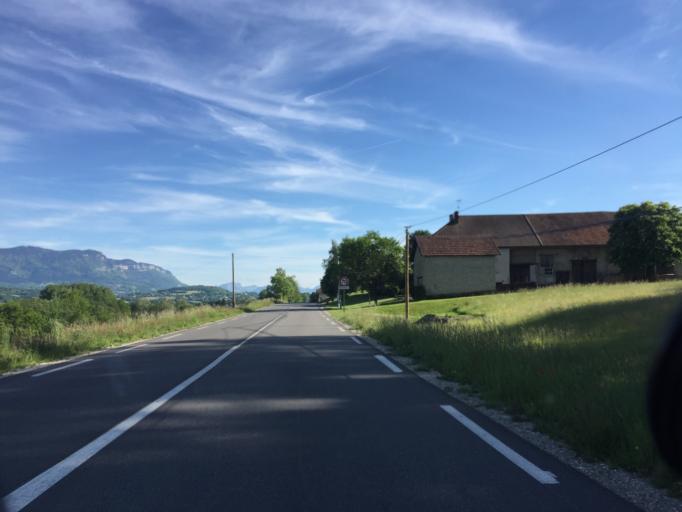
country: FR
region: Rhone-Alpes
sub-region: Departement de la Savoie
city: Albens
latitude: 45.7974
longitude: 5.9483
